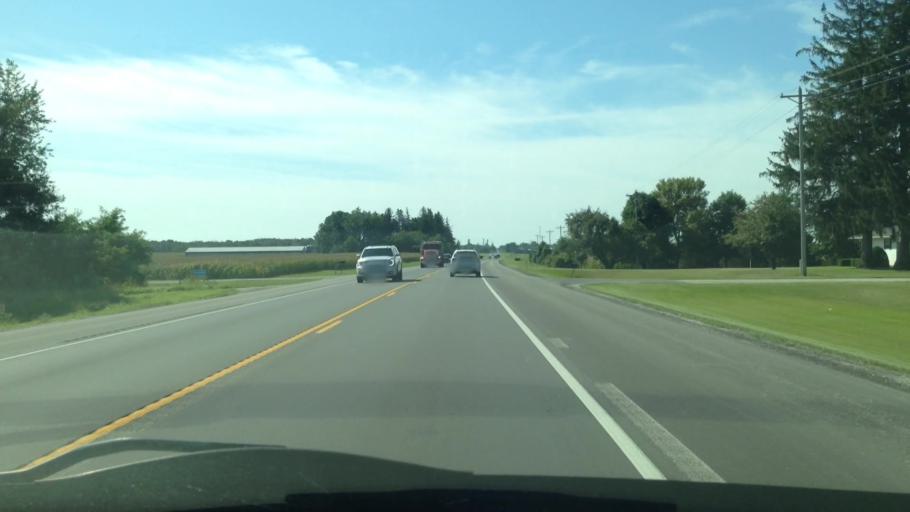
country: US
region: Minnesota
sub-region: Fillmore County
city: Harmony
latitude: 43.5806
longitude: -92.0097
